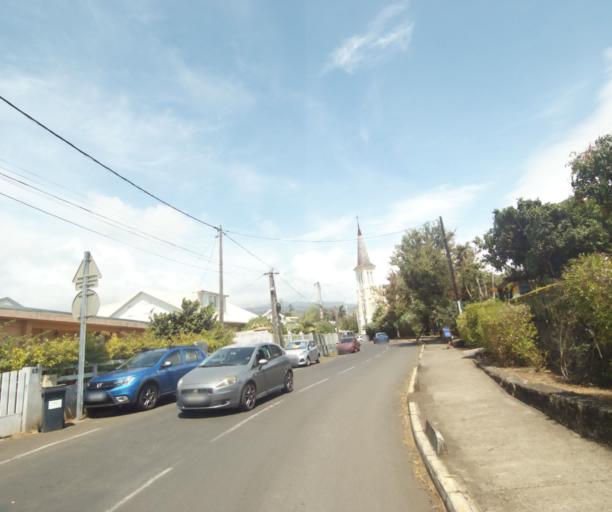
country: RE
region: Reunion
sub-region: Reunion
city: Trois-Bassins
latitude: -21.0828
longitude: 55.2684
